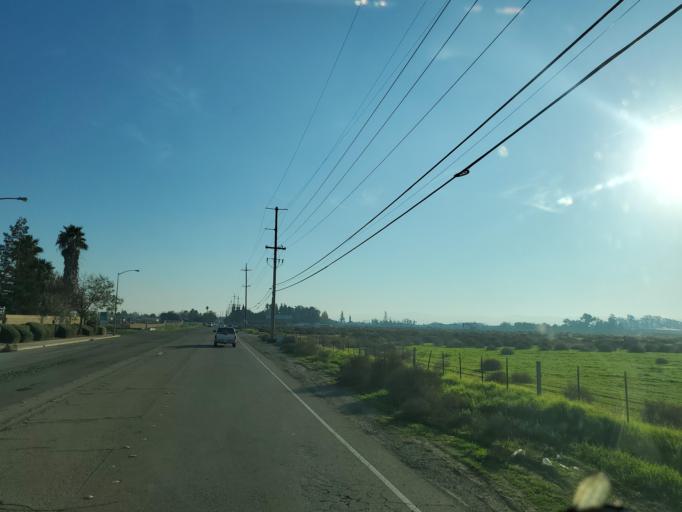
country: US
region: California
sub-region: San Joaquin County
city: Lathrop
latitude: 37.8057
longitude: -121.2527
